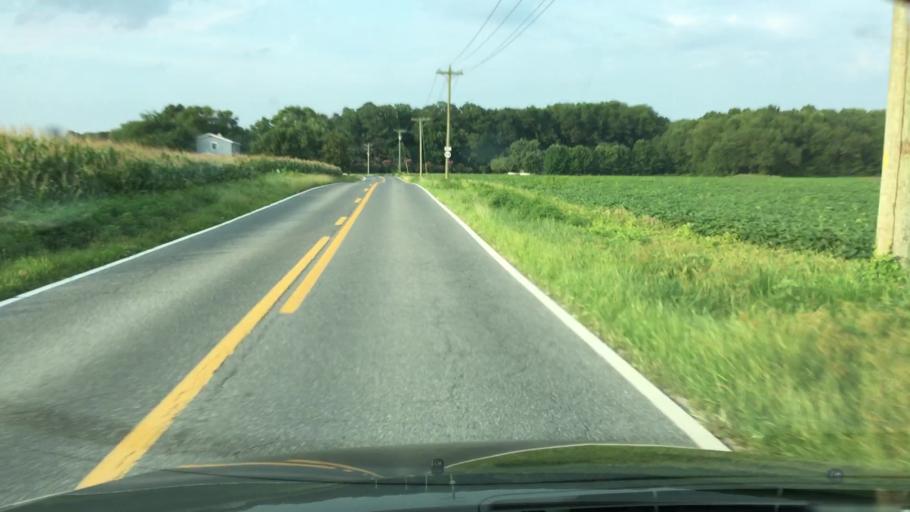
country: US
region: Delaware
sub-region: Sussex County
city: Ocean View
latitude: 38.4893
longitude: -75.1337
